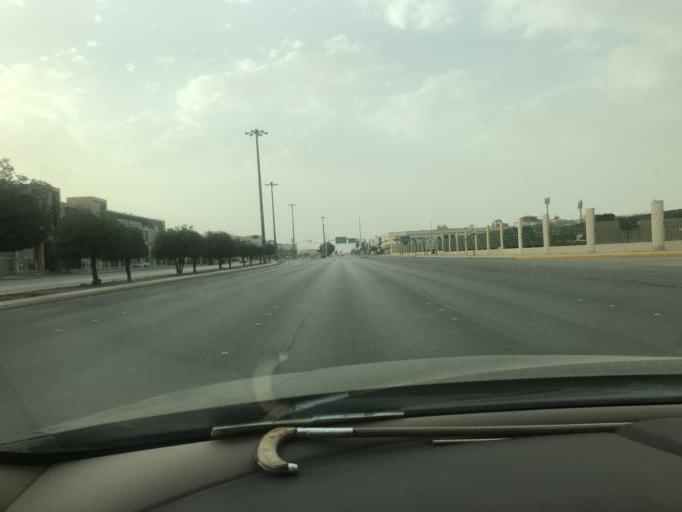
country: SA
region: Ar Riyad
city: Riyadh
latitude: 24.7919
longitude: 46.6576
